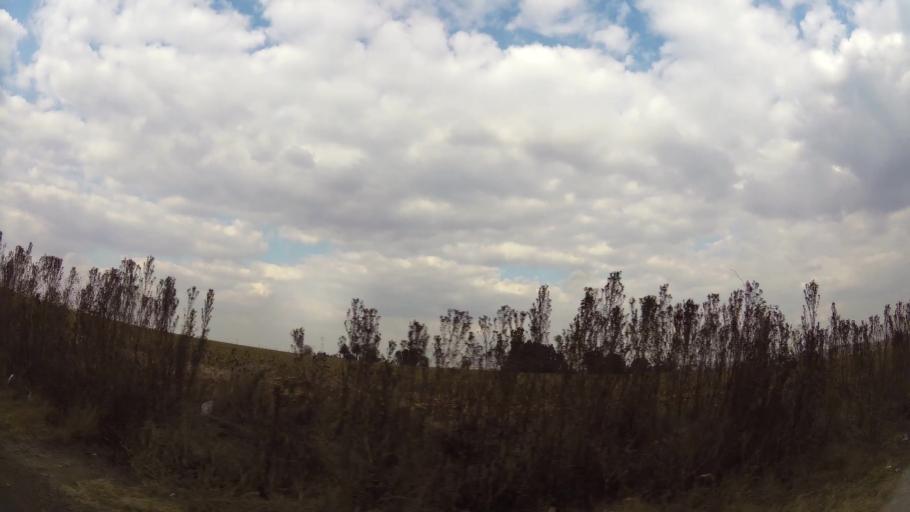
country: ZA
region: Mpumalanga
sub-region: Nkangala District Municipality
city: Delmas
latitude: -26.2602
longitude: 28.6333
